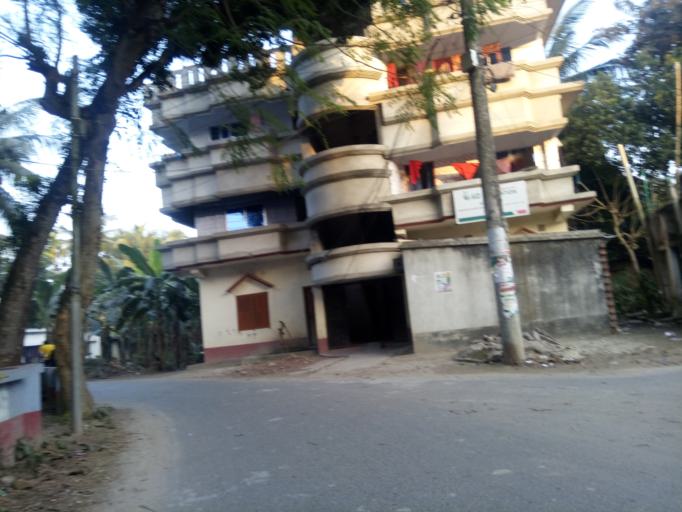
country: BD
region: Khulna
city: Kaliganj
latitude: 23.3547
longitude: 88.9216
